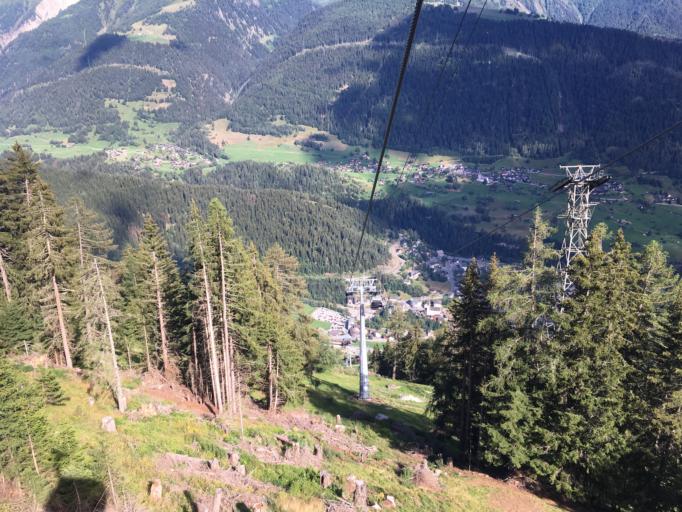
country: CH
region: Valais
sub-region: Goms District
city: Fiesch
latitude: 46.4094
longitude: 8.1202
